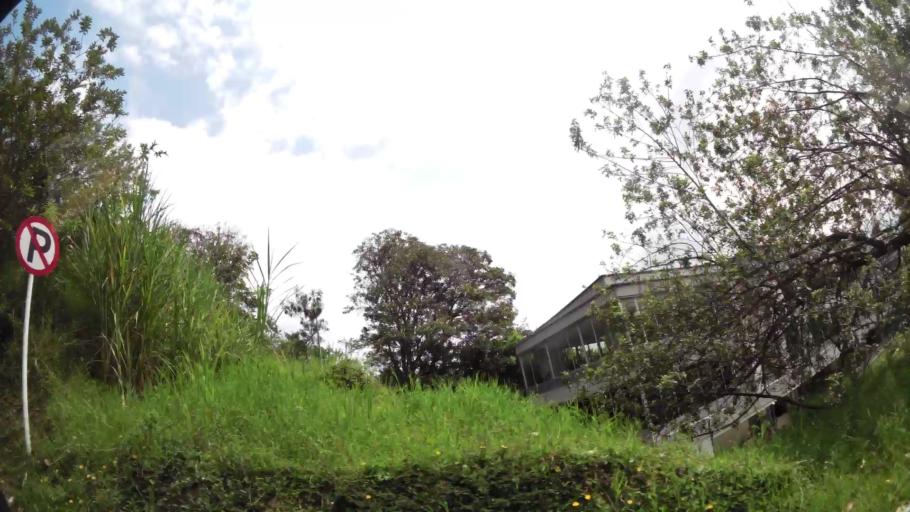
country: CO
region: Antioquia
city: Itagui
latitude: 6.1918
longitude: -75.5993
